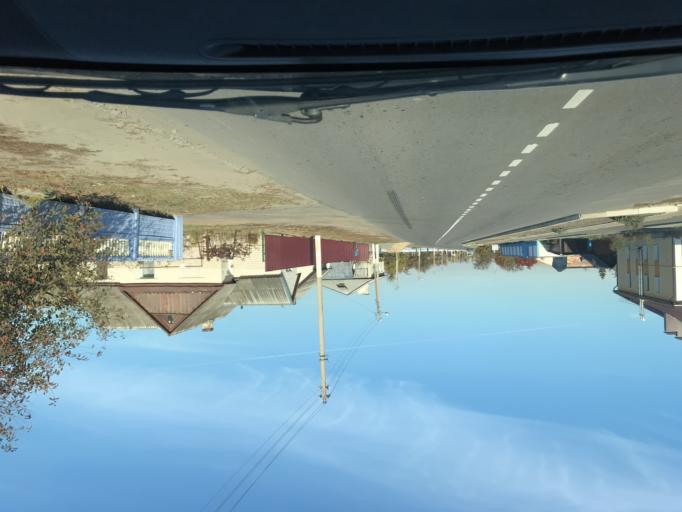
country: BY
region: Brest
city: Mikashevichy
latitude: 52.2288
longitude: 27.4574
